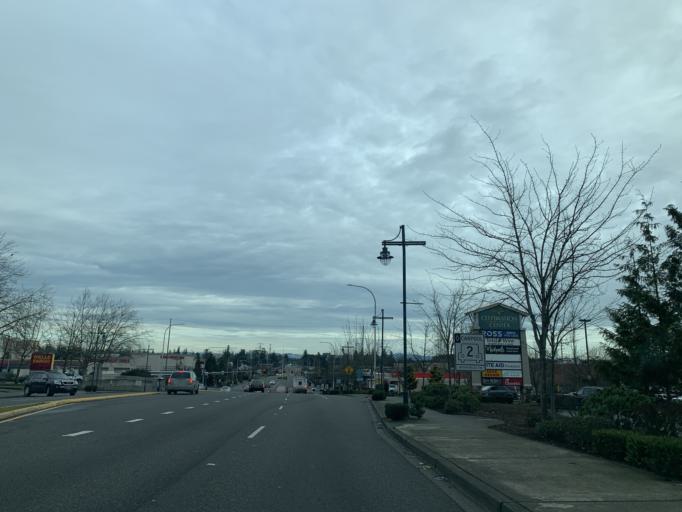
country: US
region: Washington
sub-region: King County
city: Federal Way
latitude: 47.3151
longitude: -122.3162
